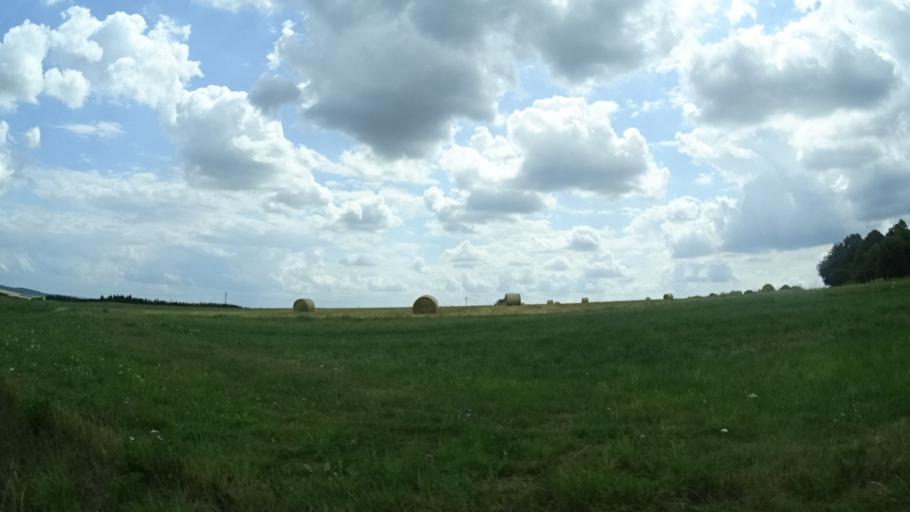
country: DE
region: Hesse
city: Gedern
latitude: 50.4251
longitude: 9.2527
